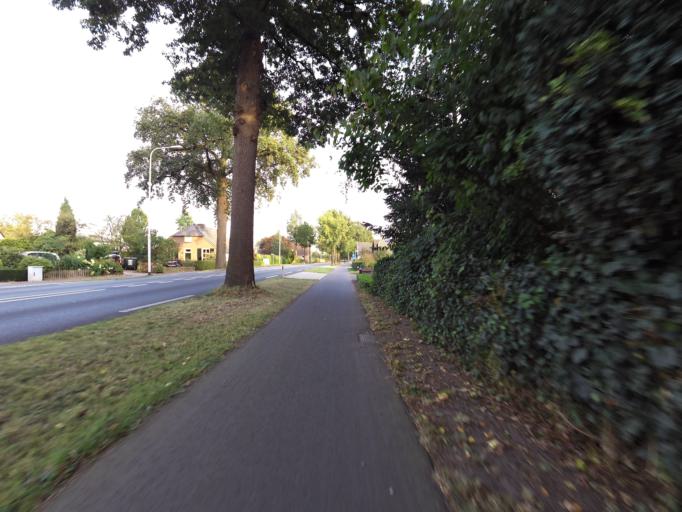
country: NL
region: Gelderland
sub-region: Gemeente Zevenaar
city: Zevenaar
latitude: 51.9113
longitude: 6.1028
